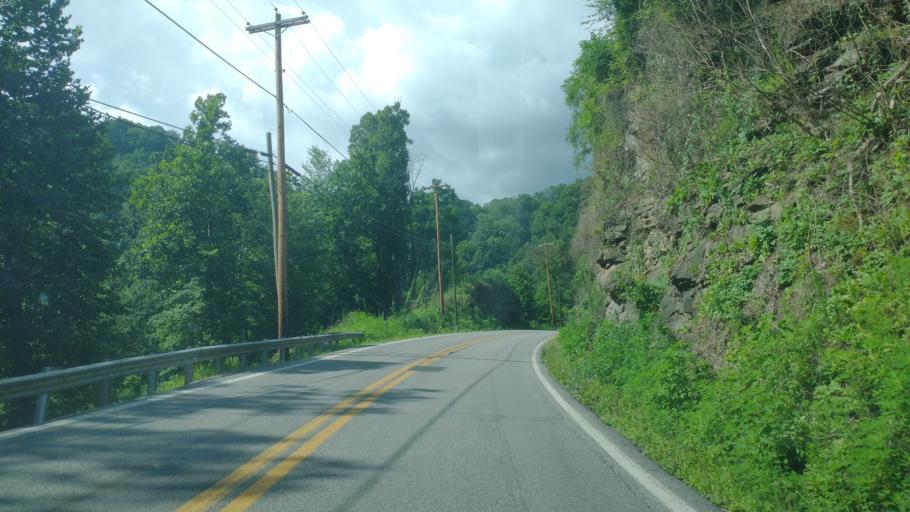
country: US
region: West Virginia
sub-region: McDowell County
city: Welch
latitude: 37.4223
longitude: -81.5113
